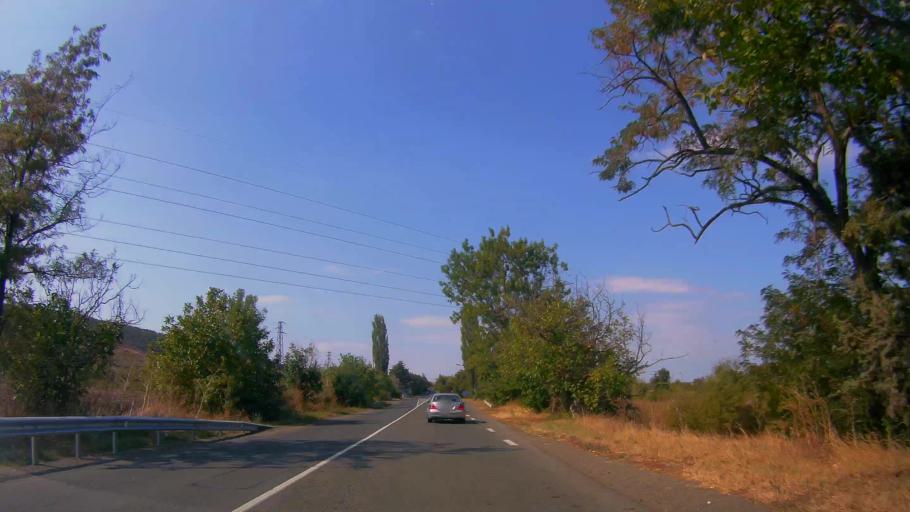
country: BG
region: Burgas
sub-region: Obshtina Karnobat
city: Karnobat
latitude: 42.6540
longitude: 27.0084
